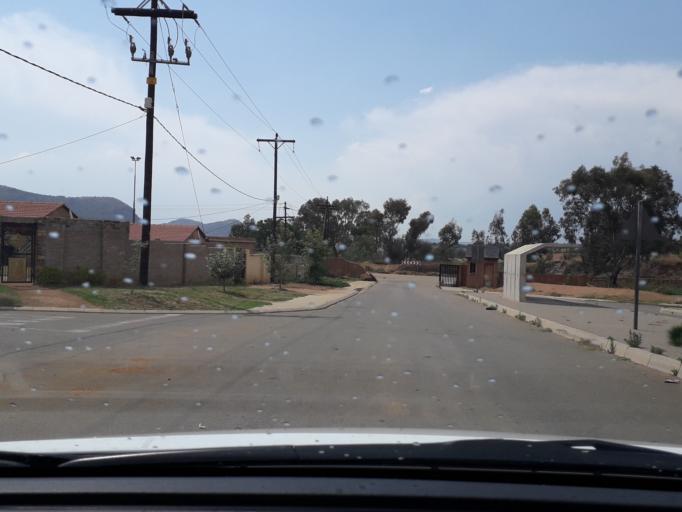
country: ZA
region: Gauteng
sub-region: West Rand District Municipality
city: Muldersdriseloop
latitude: -26.0048
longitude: 27.8529
